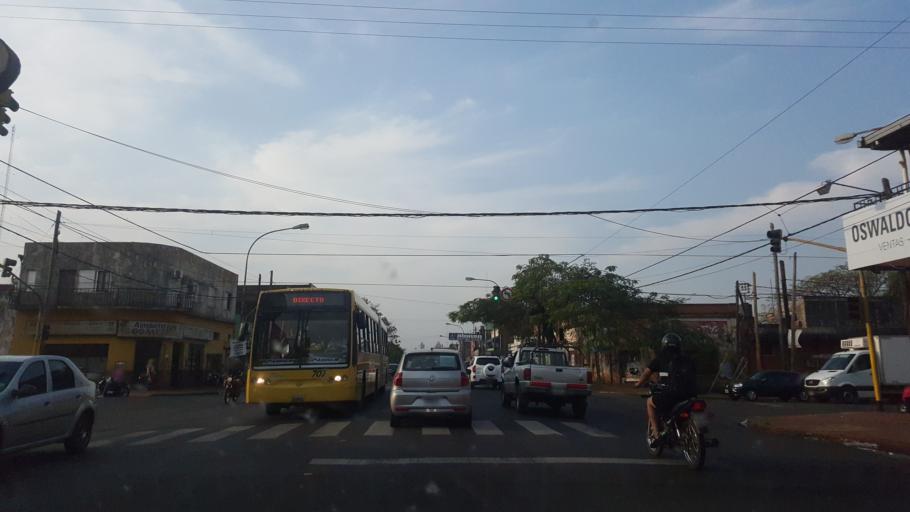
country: AR
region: Misiones
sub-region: Departamento de Capital
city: Posadas
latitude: -27.3879
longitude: -55.9004
